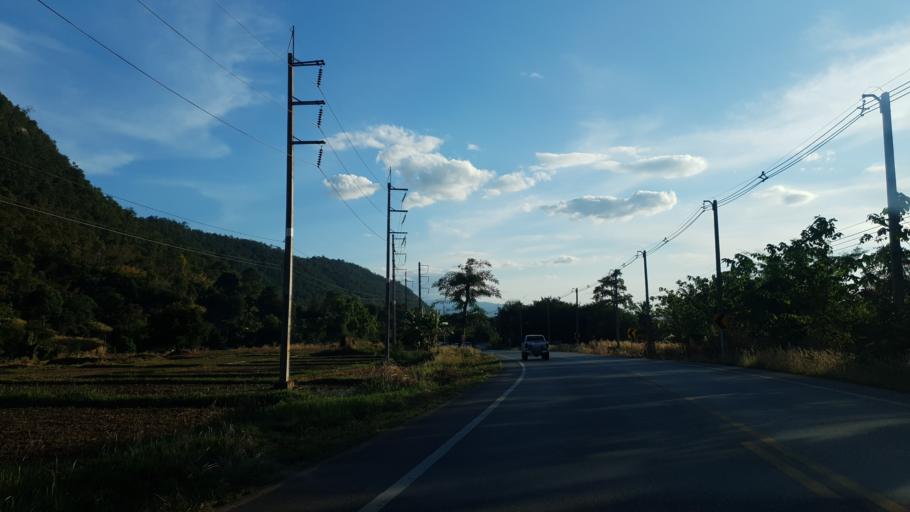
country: TH
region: Loei
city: Dan Sai
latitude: 17.2084
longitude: 101.0164
